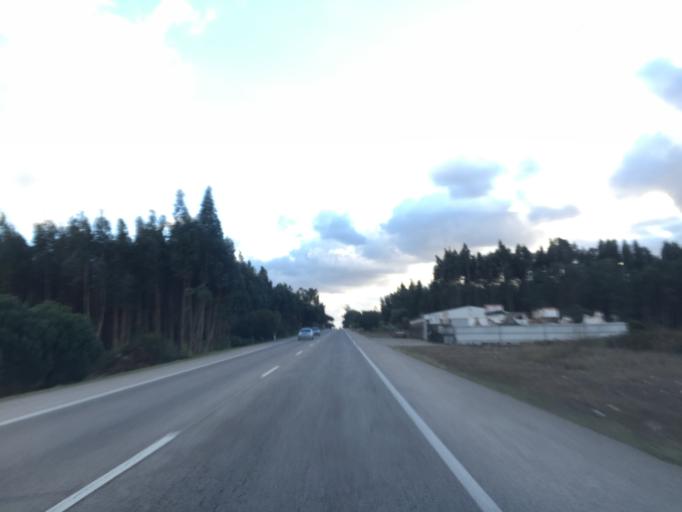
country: PT
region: Leiria
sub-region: Alcobaca
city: Turquel
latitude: 39.4765
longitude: -8.9386
